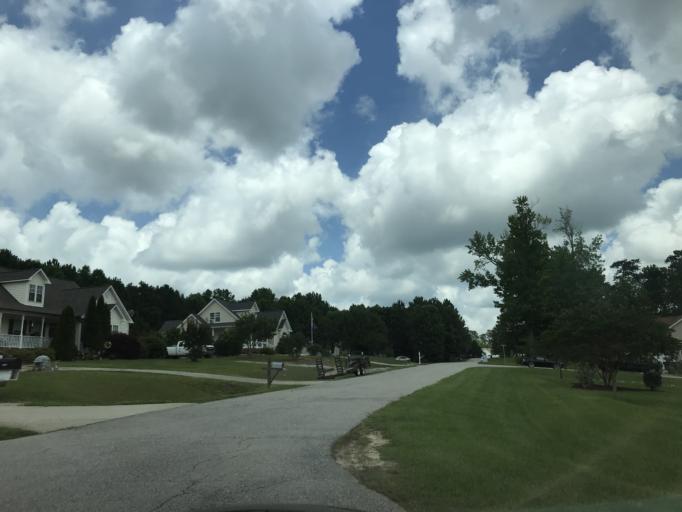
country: US
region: North Carolina
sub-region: Wake County
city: Rolesville
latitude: 35.9477
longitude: -78.3748
